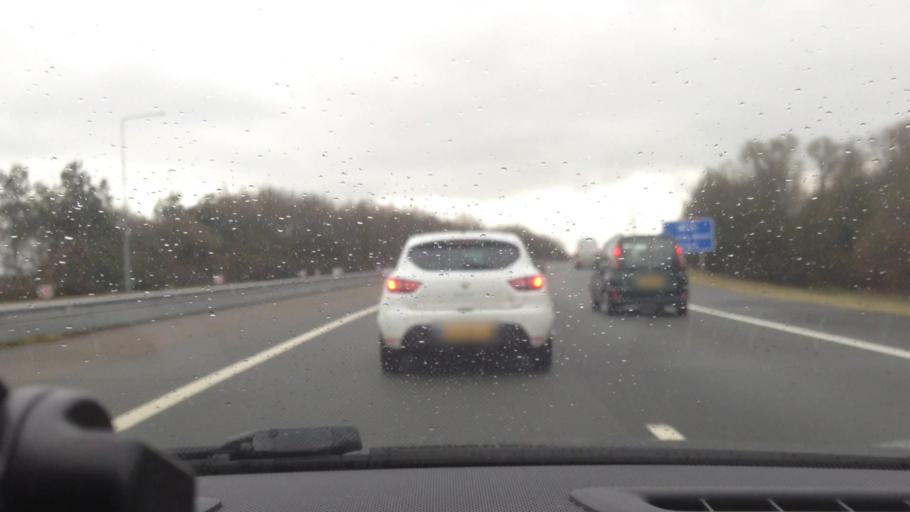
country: NL
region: Overijssel
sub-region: Gemeente Borne
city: Borne
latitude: 52.2829
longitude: 6.7442
